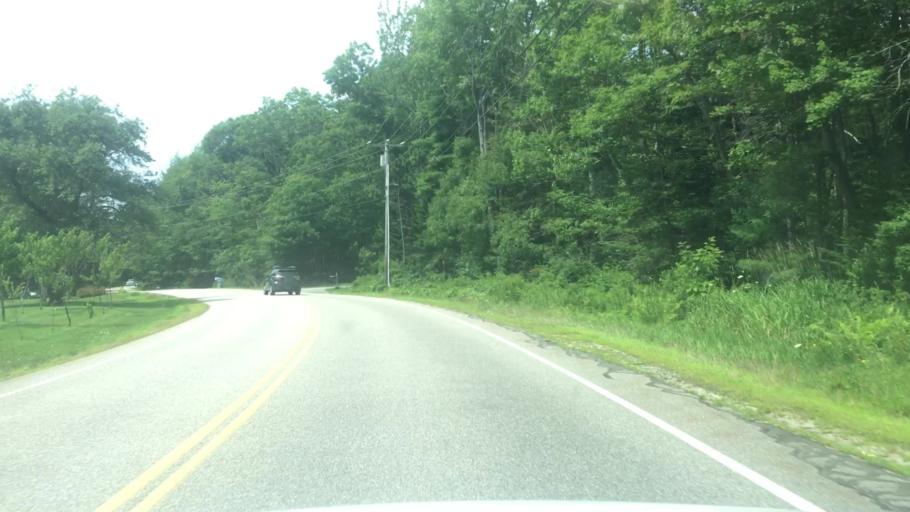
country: US
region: Maine
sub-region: Cumberland County
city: Scarborough
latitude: 43.5762
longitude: -70.2834
